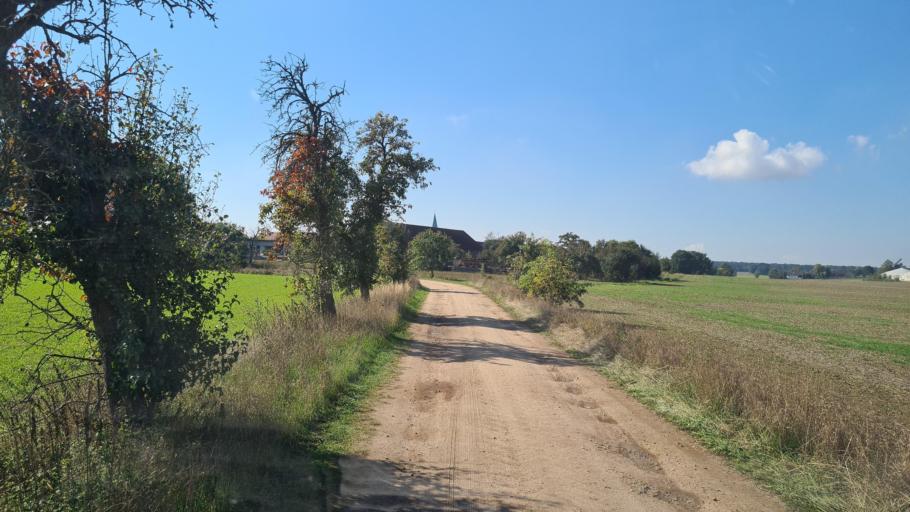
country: DE
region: Brandenburg
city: Lebusa
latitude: 51.8270
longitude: 13.4603
